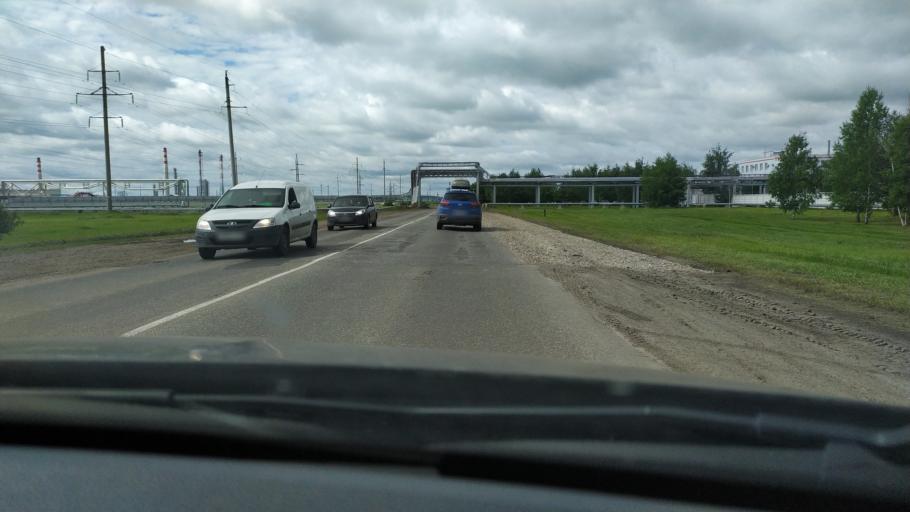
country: RU
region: Perm
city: Kondratovo
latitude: 57.9304
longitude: 56.1223
